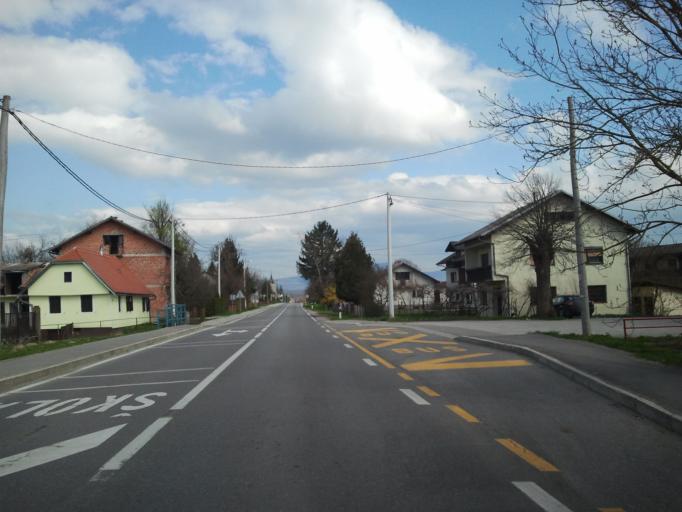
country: HR
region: Zagrebacka
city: Jastrebarsko
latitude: 45.6031
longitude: 15.5984
